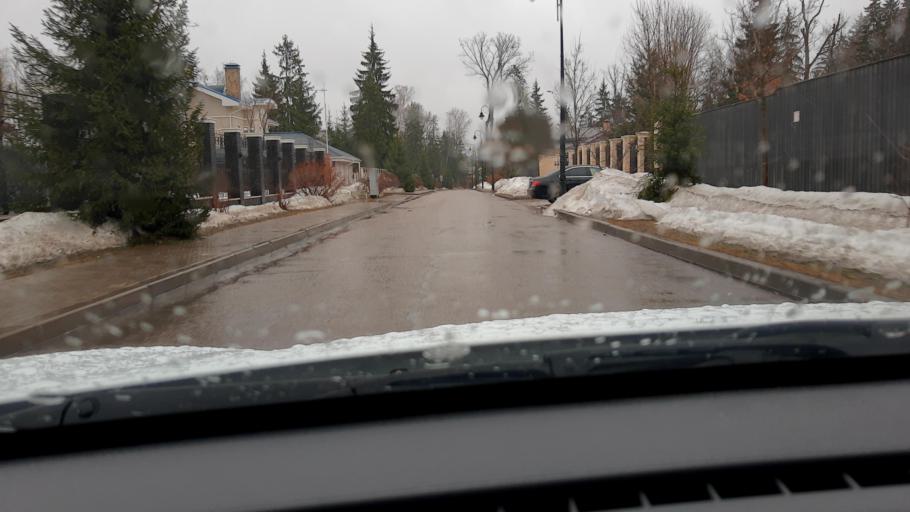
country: RU
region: Moskovskaya
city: Moskovskiy
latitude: 55.5811
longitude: 37.3953
